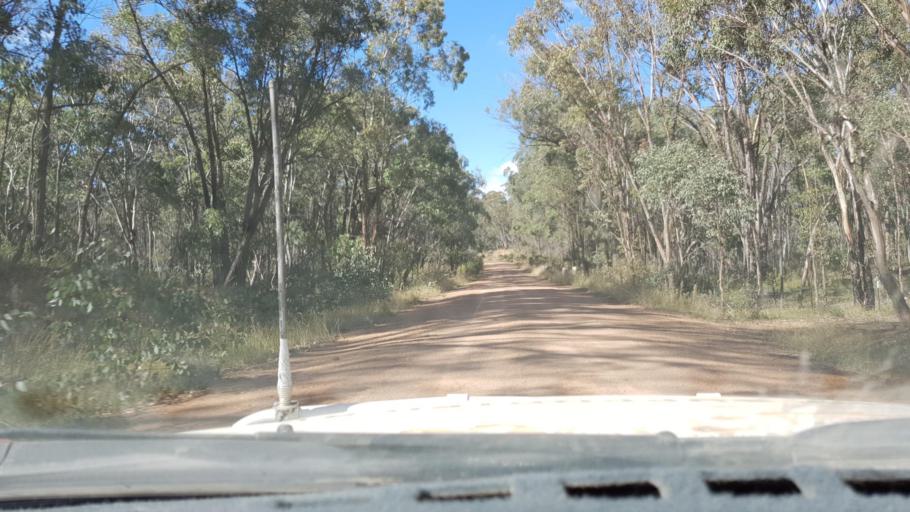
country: AU
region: New South Wales
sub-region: Tamworth Municipality
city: Manilla
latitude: -30.4562
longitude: 150.8809
